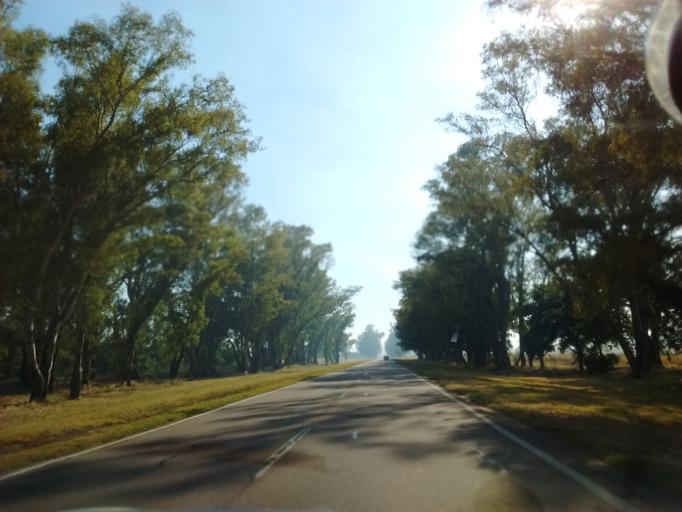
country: AR
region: La Pampa
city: Santa Rosa
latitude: -36.5718
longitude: -64.1484
